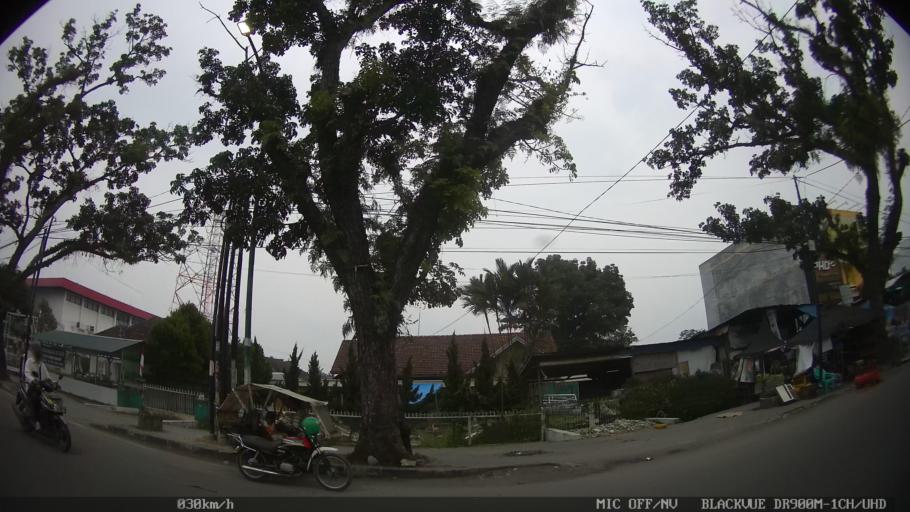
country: ID
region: North Sumatra
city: Medan
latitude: 3.5684
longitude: 98.7003
